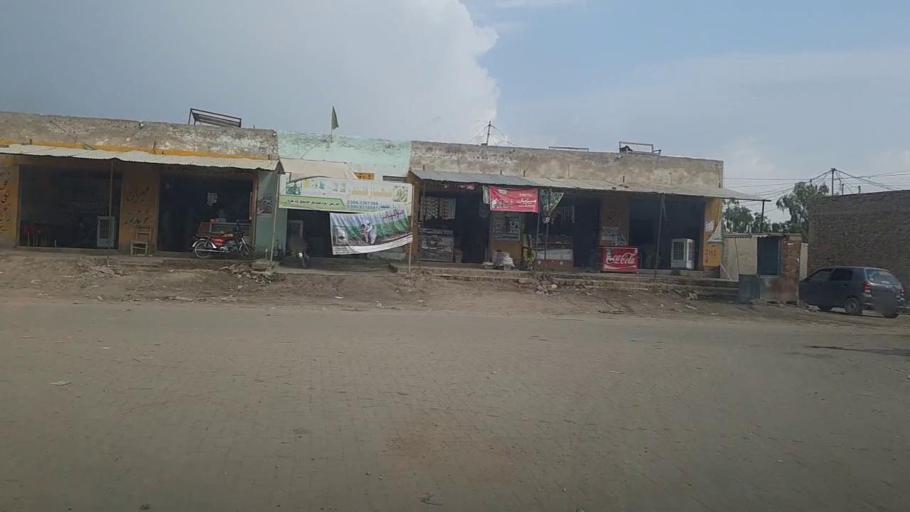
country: PK
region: Sindh
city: Mirpur Mathelo
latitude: 27.9170
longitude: 69.5218
